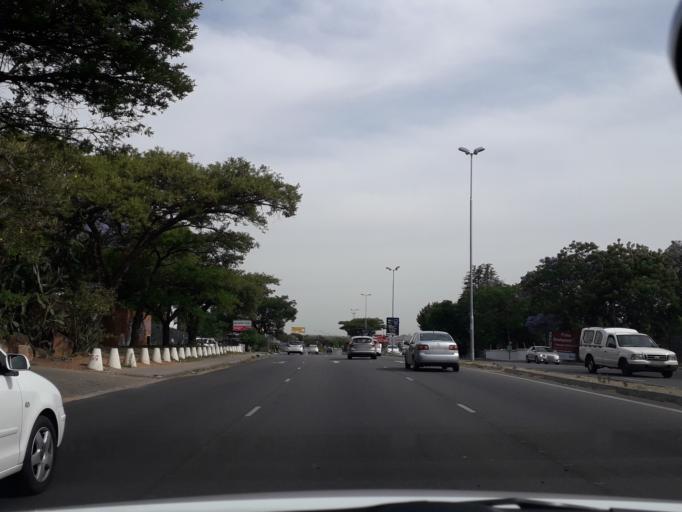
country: ZA
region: Gauteng
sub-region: City of Johannesburg Metropolitan Municipality
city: Diepsloot
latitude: -26.0543
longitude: 28.0219
